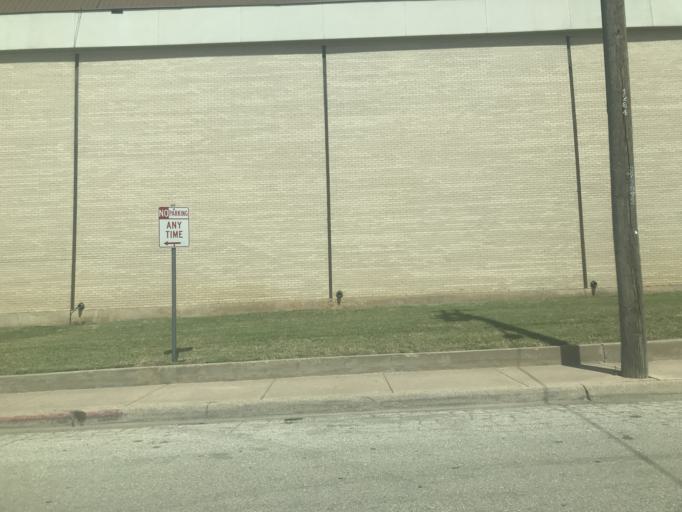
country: US
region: Texas
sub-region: Taylor County
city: Abilene
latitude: 32.4309
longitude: -99.7524
